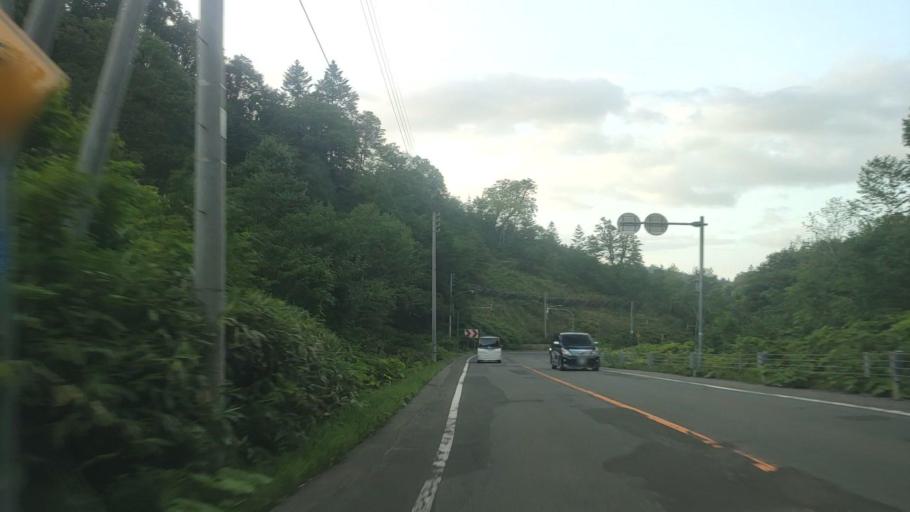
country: JP
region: Hokkaido
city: Bibai
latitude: 43.2920
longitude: 142.0764
